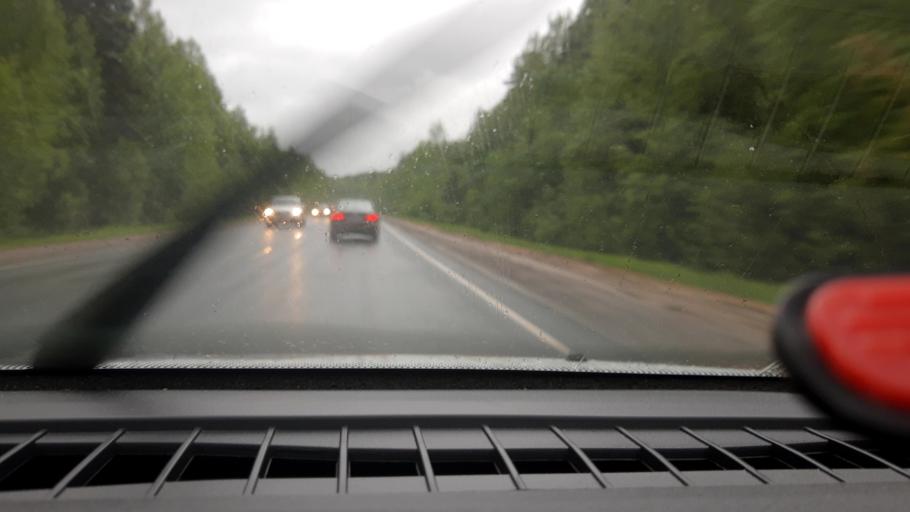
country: RU
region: Nizjnij Novgorod
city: Semenov
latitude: 56.7641
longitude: 44.3932
